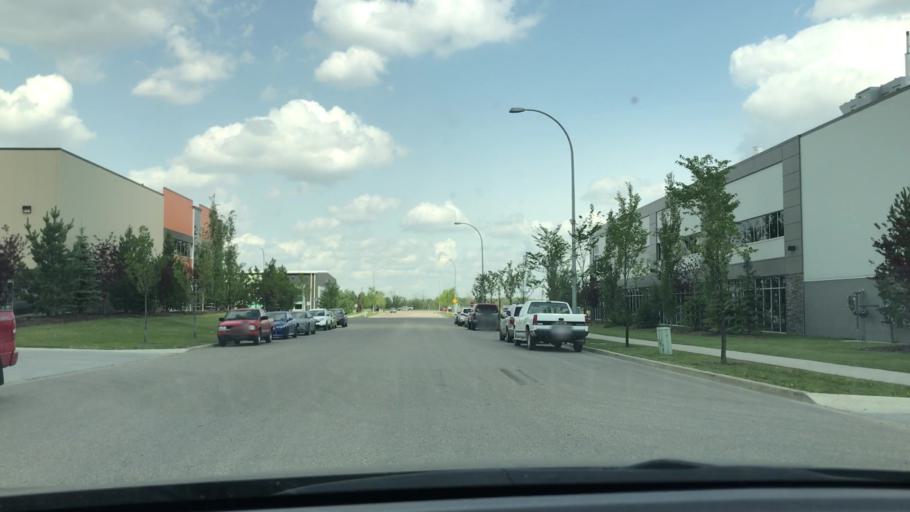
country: CA
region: Alberta
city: Edmonton
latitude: 53.4942
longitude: -113.4060
